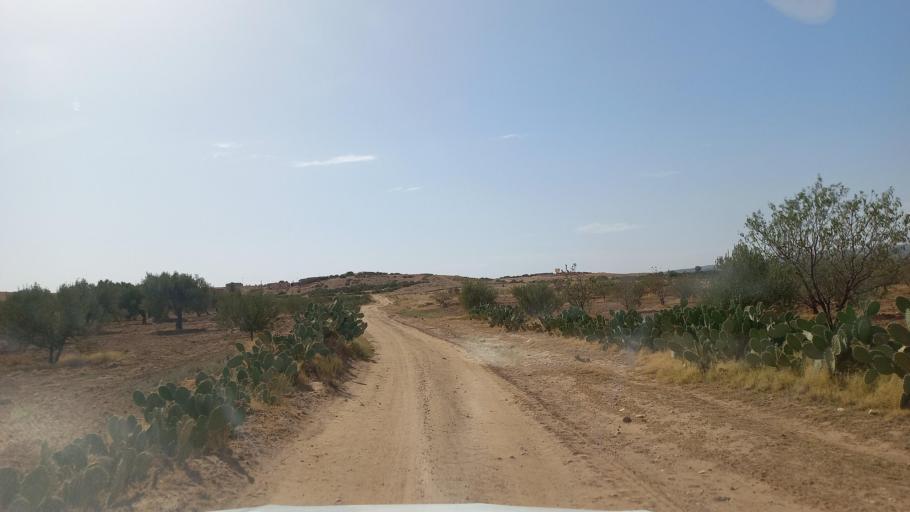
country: TN
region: Al Qasrayn
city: Kasserine
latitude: 35.2726
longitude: 8.9589
